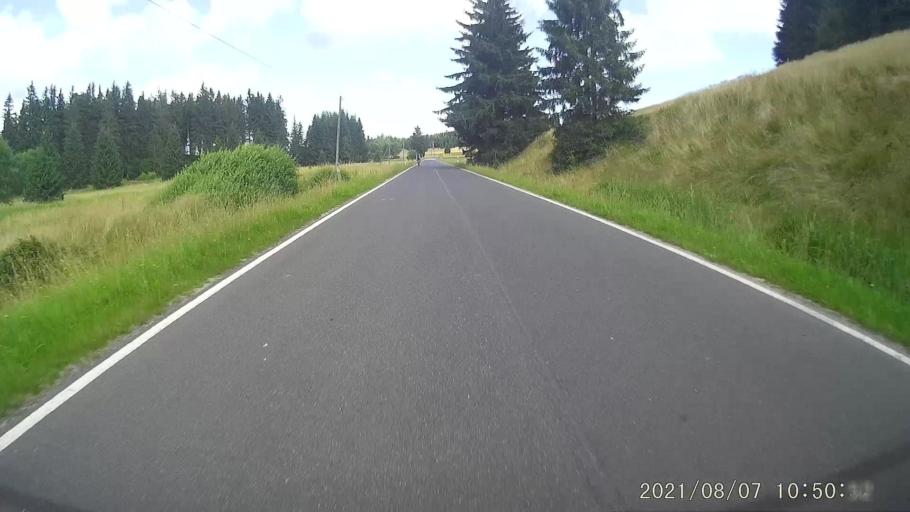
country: PL
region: Lower Silesian Voivodeship
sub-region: Powiat klodzki
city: Polanica-Zdroj
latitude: 50.2938
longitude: 16.4665
